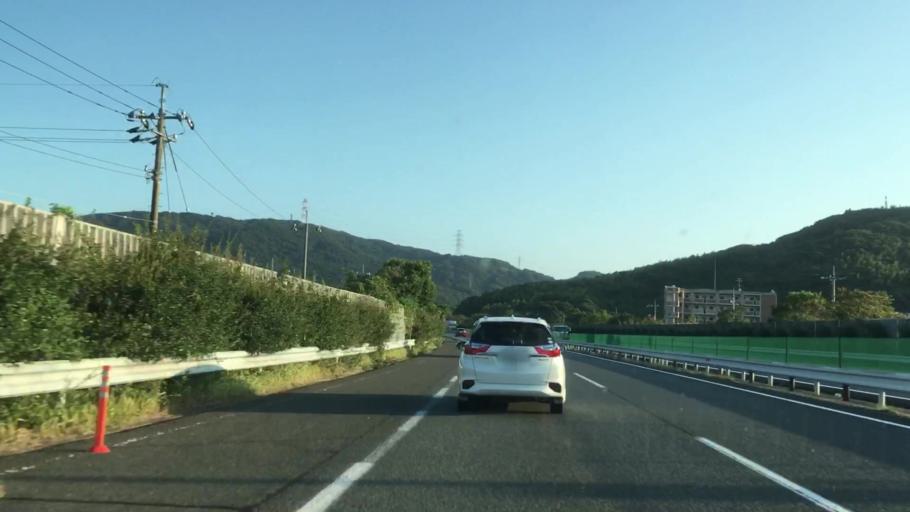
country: JP
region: Yamaguchi
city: Shimonoseki
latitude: 34.0105
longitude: 130.9555
